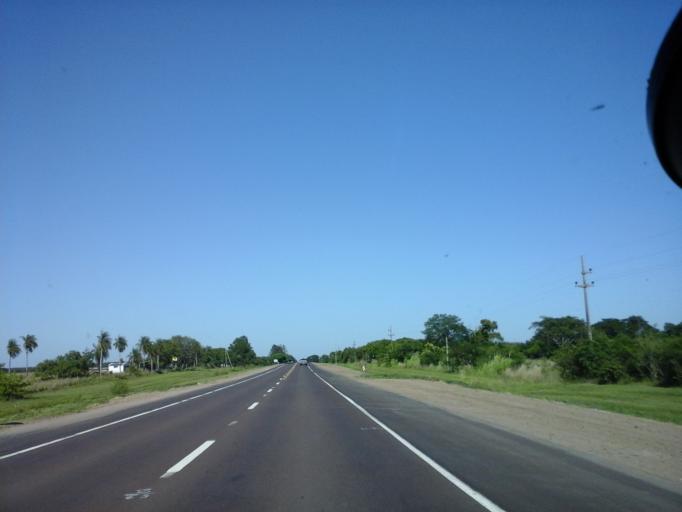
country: AR
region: Corrientes
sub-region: Departamento de San Cosme
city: San Cosme
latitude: -27.3676
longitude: -58.3786
